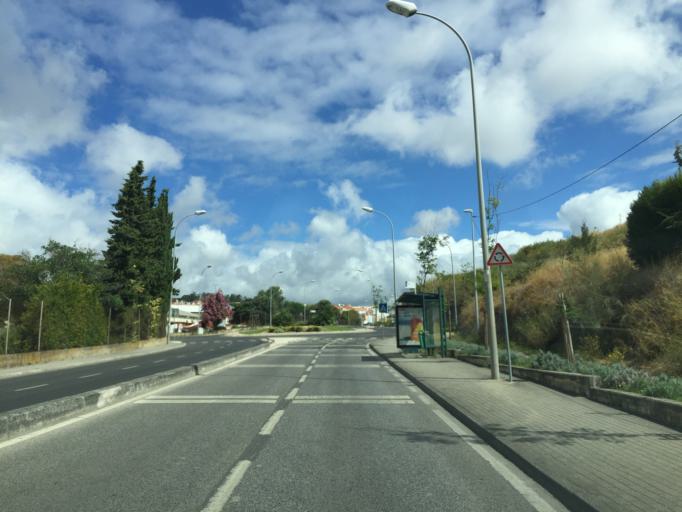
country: PT
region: Lisbon
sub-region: Amadora
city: Amadora
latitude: 38.7735
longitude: -9.2306
